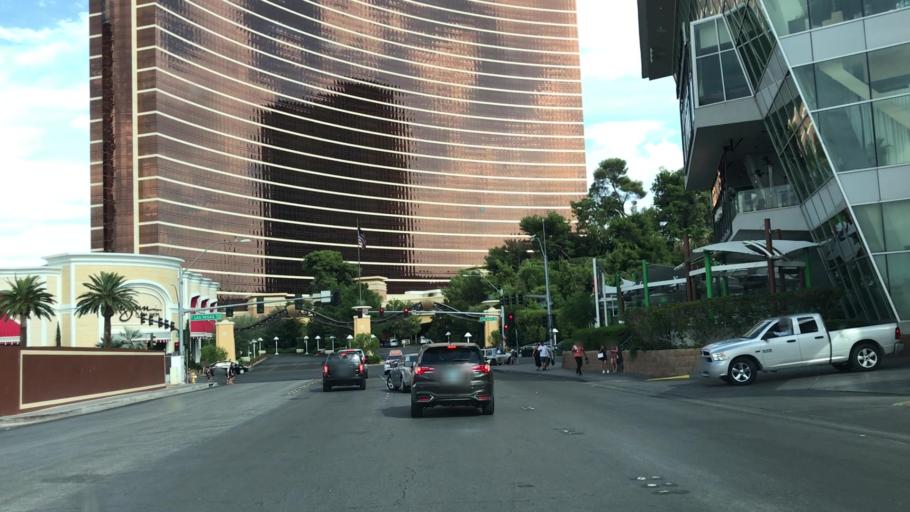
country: US
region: Nevada
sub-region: Clark County
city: Paradise
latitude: 36.1281
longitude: -115.1688
